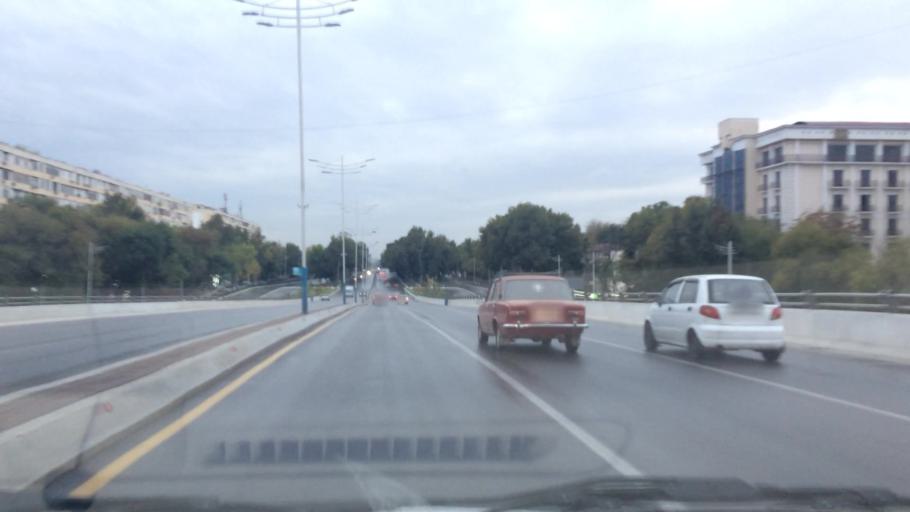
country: UZ
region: Toshkent Shahri
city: Tashkent
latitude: 41.2915
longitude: 69.2228
